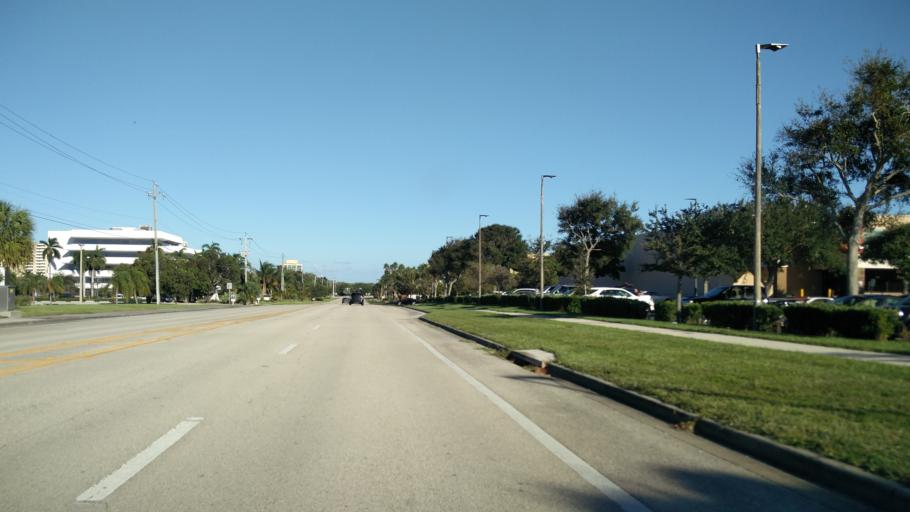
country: US
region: Florida
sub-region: Palm Beach County
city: Jupiter
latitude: 26.9339
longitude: -80.0784
